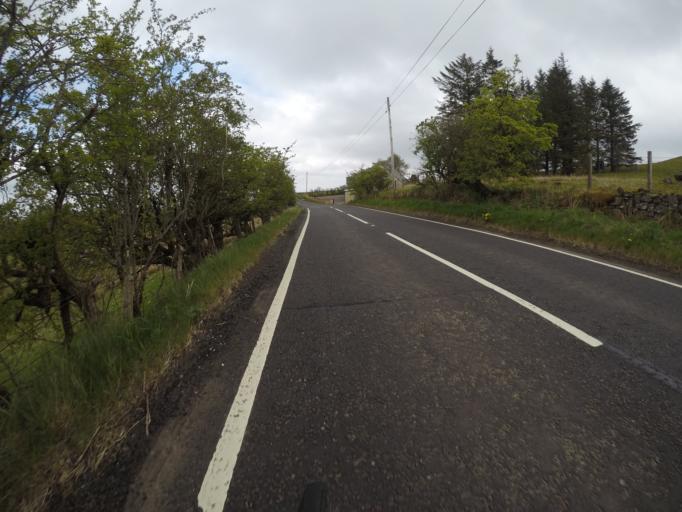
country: GB
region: Scotland
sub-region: East Renfrewshire
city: Barrhead
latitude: 55.7532
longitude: -4.3858
